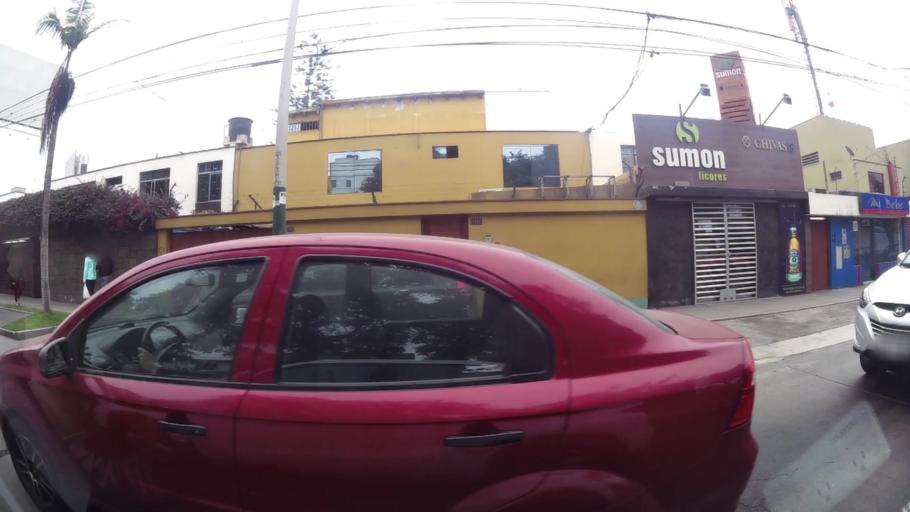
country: PE
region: Lima
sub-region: Lima
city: Surco
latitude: -12.1280
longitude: -76.9890
